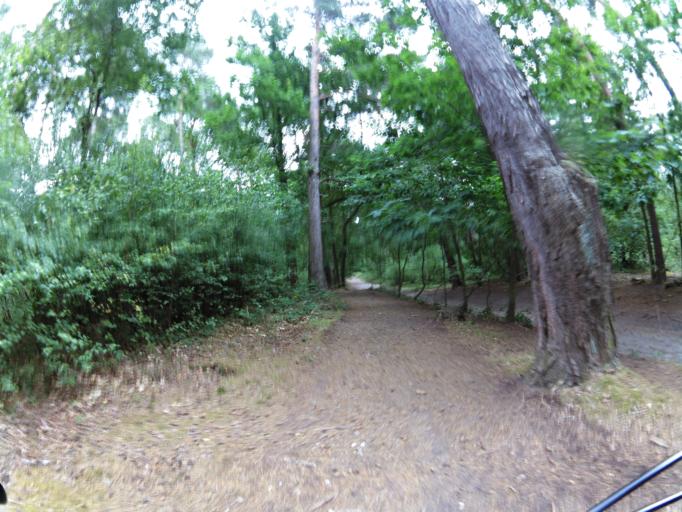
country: NL
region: Limburg
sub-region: Gemeente Brunssum
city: Brunssum
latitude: 50.9188
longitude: 5.9885
